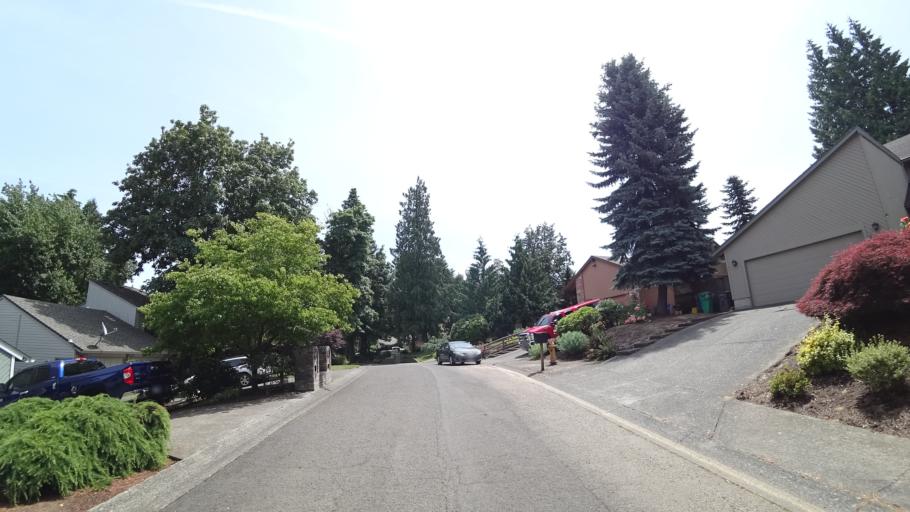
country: US
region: Oregon
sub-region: Multnomah County
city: Fairview
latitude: 45.5443
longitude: -122.4946
